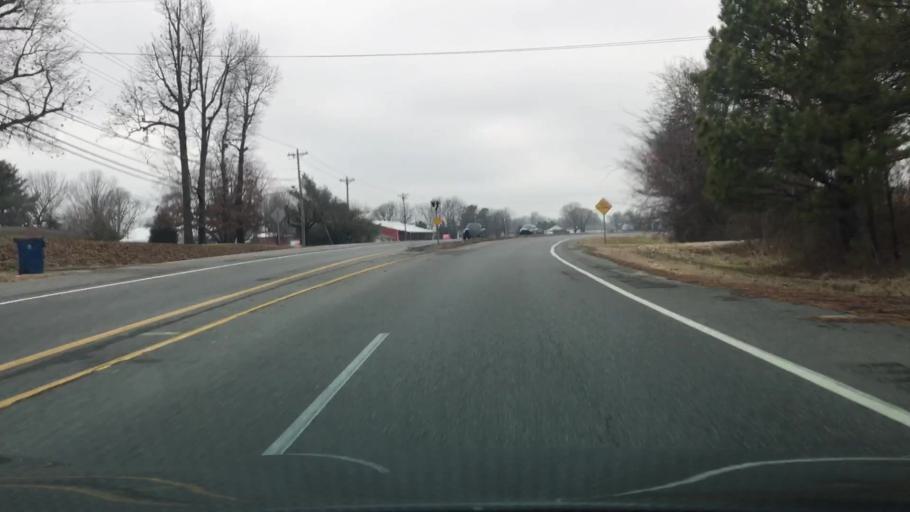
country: US
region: Kentucky
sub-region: McCracken County
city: Reidland
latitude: 36.9877
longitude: -88.5027
